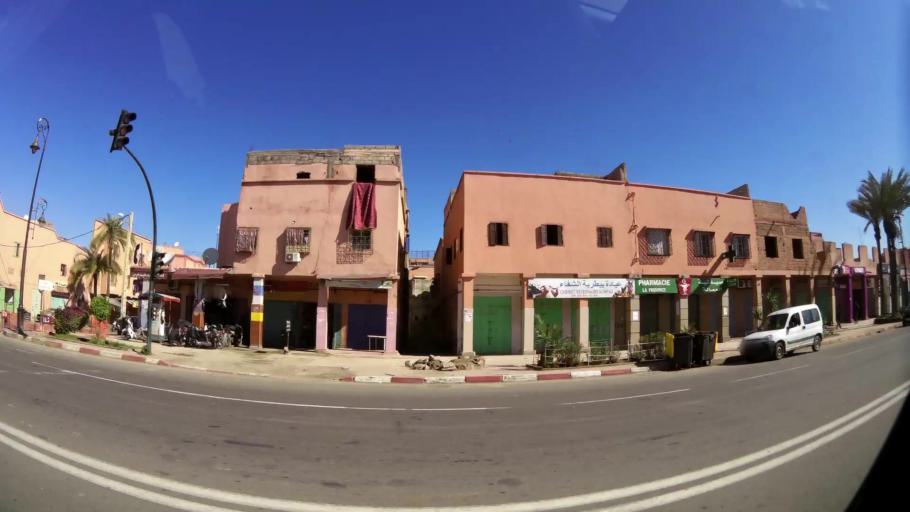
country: MA
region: Marrakech-Tensift-Al Haouz
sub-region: Marrakech
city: Marrakesh
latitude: 31.6450
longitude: -7.9819
